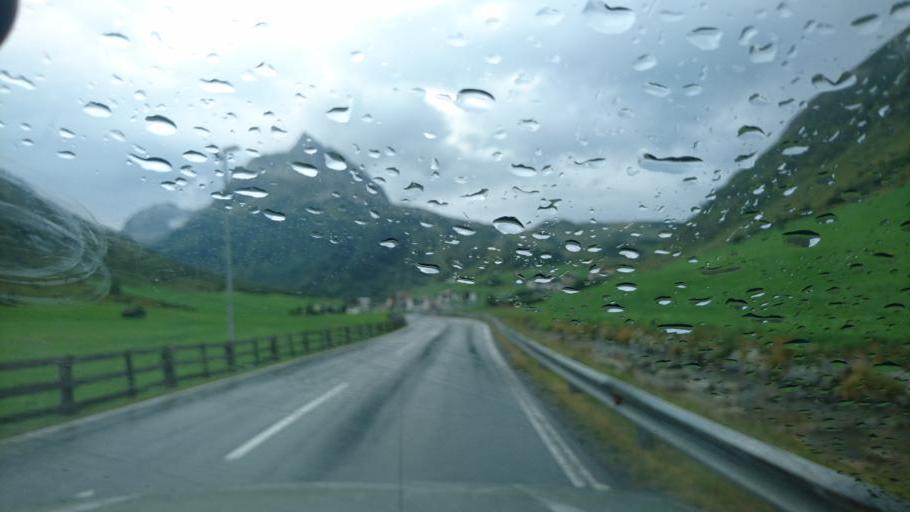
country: AT
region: Tyrol
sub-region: Politischer Bezirk Landeck
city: Galtur
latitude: 46.9671
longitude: 10.1723
